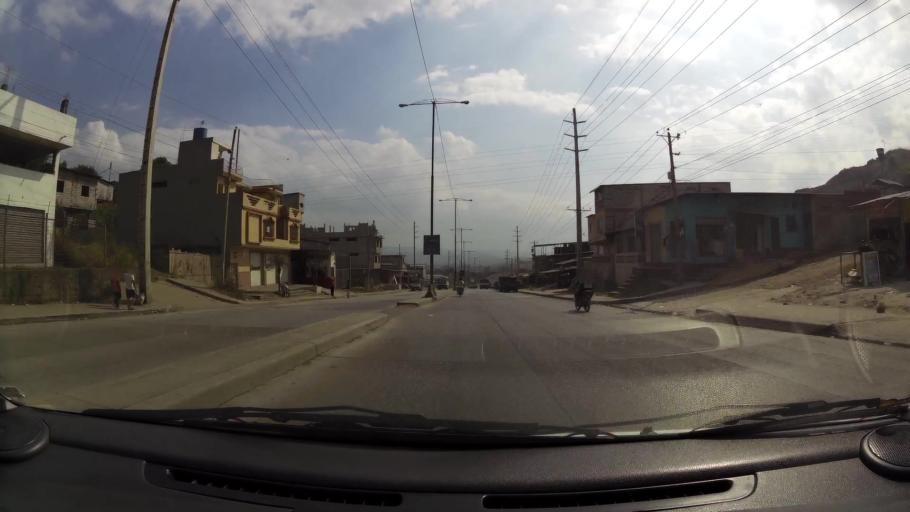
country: EC
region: Guayas
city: Santa Lucia
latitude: -2.1205
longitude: -79.9712
